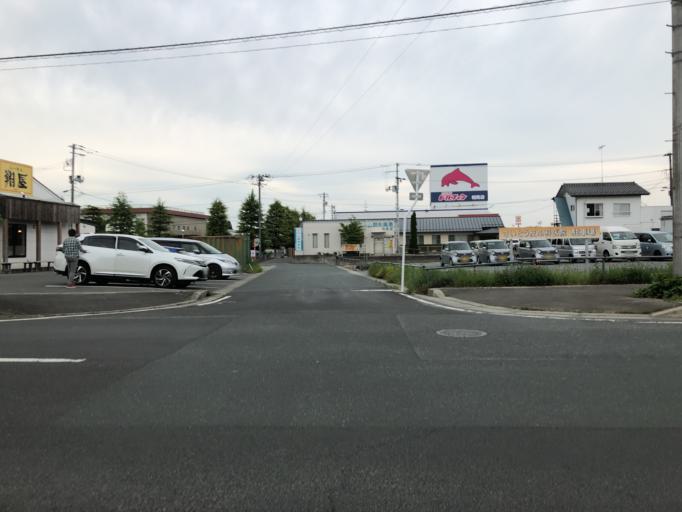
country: JP
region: Miyagi
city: Marumori
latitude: 37.8038
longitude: 140.9275
